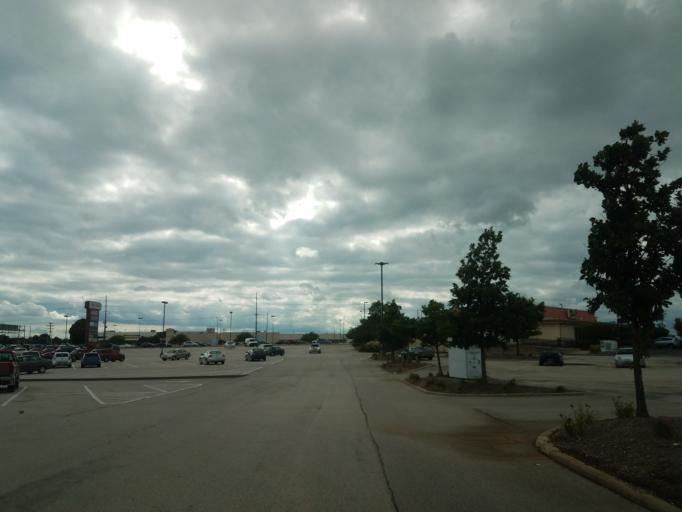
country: US
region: Illinois
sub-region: McLean County
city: Bloomington
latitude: 40.4863
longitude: -88.9506
